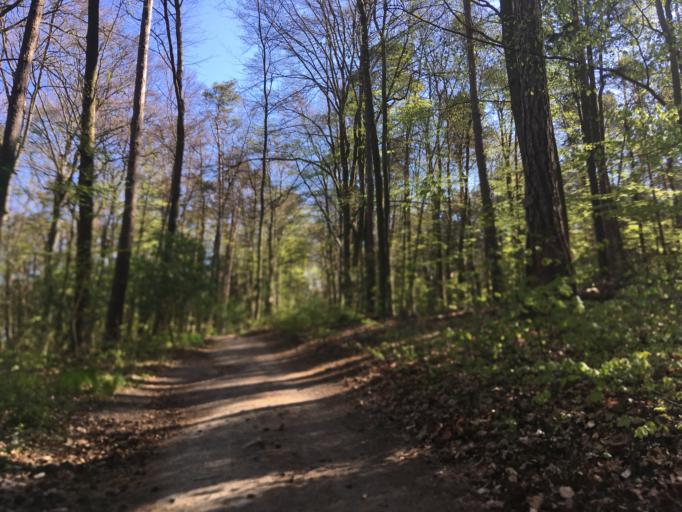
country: DE
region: Brandenburg
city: Wandlitz
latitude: 52.7535
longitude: 13.5299
